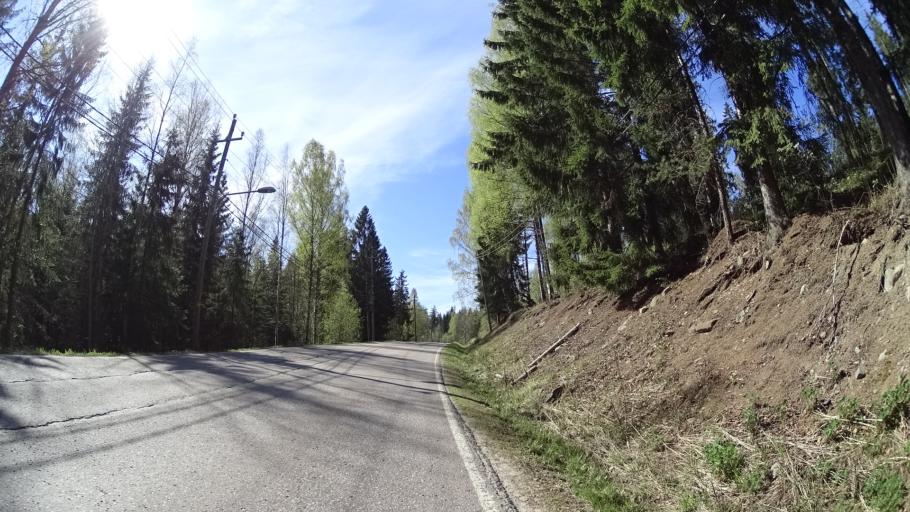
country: FI
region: Uusimaa
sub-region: Helsinki
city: Nurmijaervi
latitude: 60.3887
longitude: 24.8369
